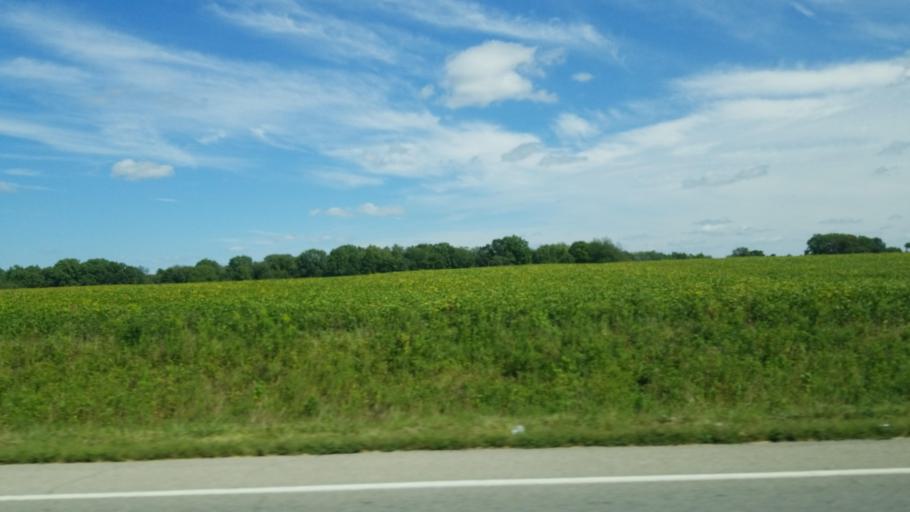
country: US
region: Illinois
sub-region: Williamson County
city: Marion
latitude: 37.7691
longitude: -88.9328
